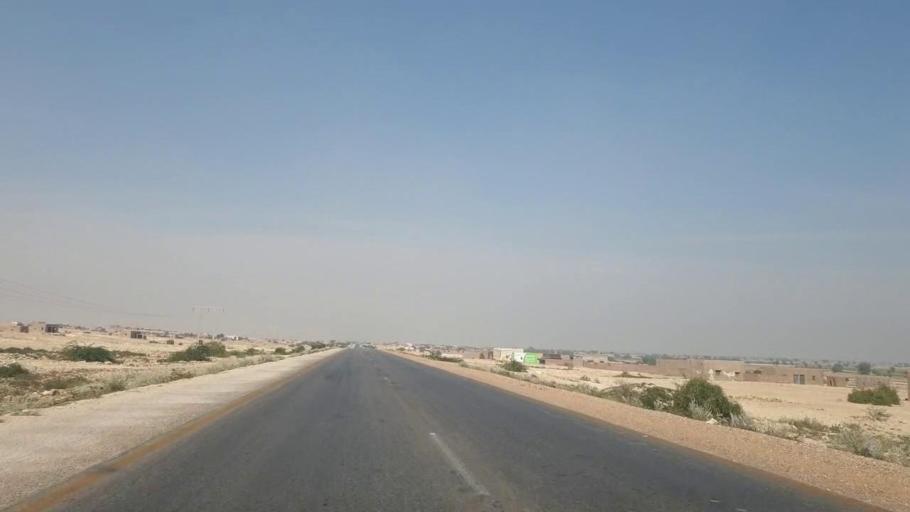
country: PK
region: Sindh
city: Hala
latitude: 25.7805
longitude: 68.2844
